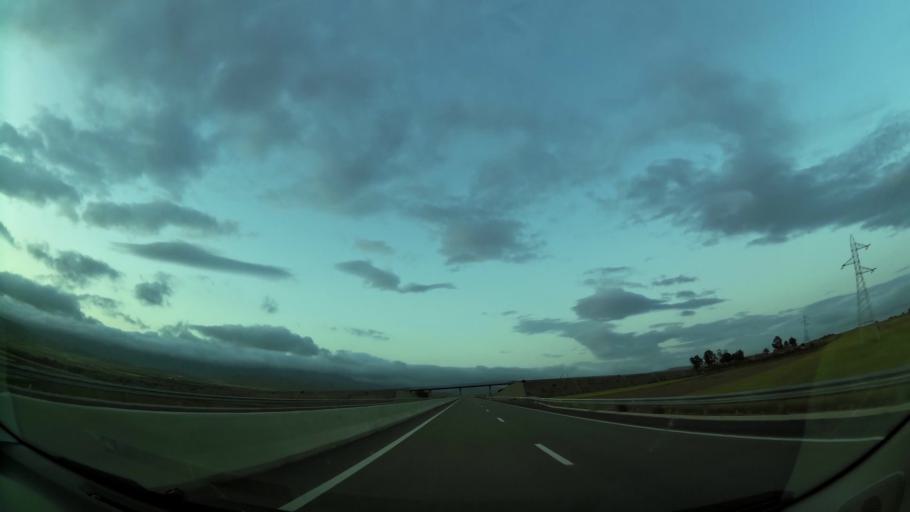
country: MA
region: Oriental
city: El Aioun
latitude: 34.6165
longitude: -2.5520
